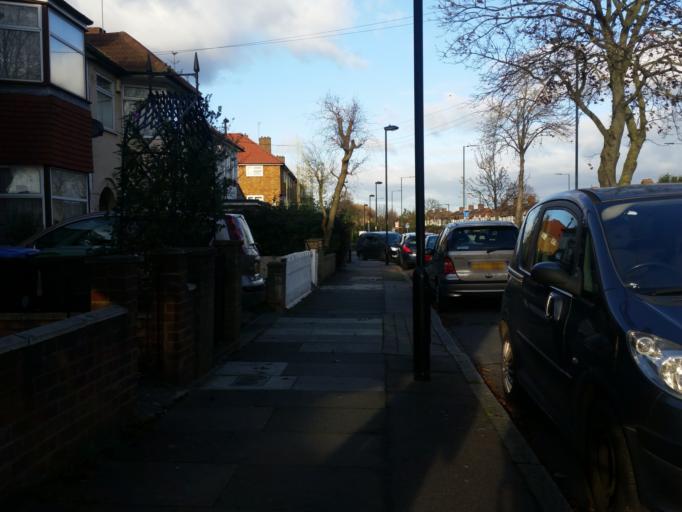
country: GB
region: England
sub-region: Greater London
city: Enfield
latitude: 51.6215
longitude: -0.0832
